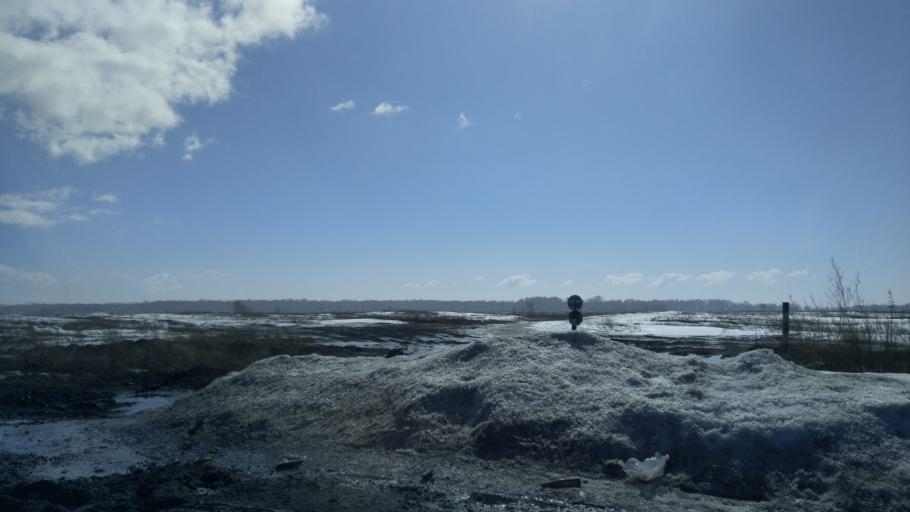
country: RU
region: Kemerovo
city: Yurga
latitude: 55.6834
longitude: 85.0038
